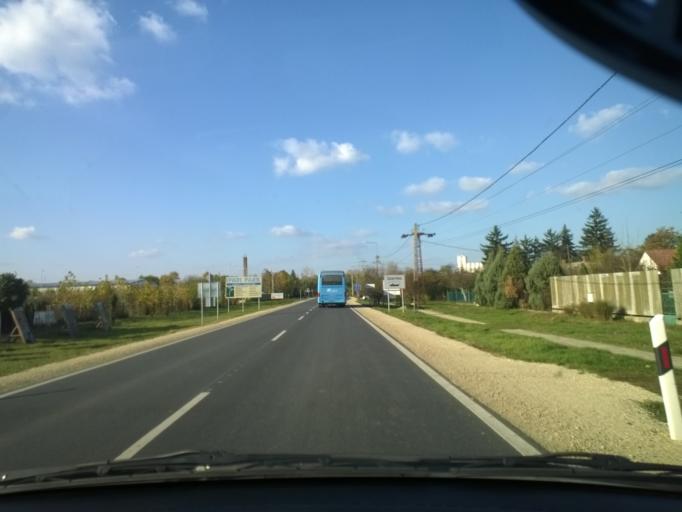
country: HU
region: Csongrad
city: Szentes
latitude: 46.6296
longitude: 20.2759
